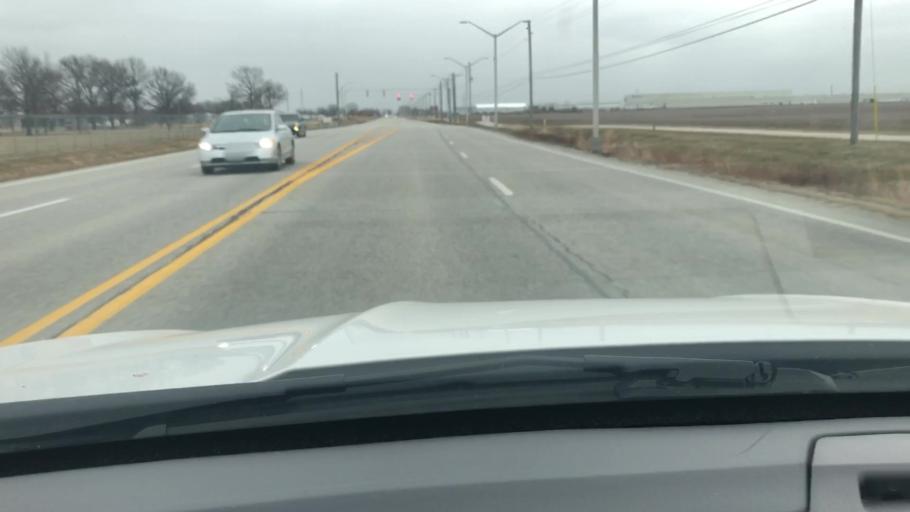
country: US
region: Indiana
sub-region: Tippecanoe County
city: Lafayette
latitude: 40.3673
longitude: -86.8467
